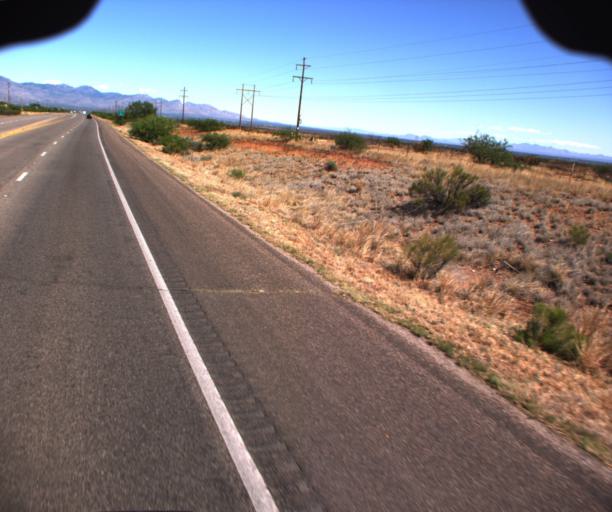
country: US
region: Arizona
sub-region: Cochise County
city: Huachuca City
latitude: 31.5916
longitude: -110.3233
